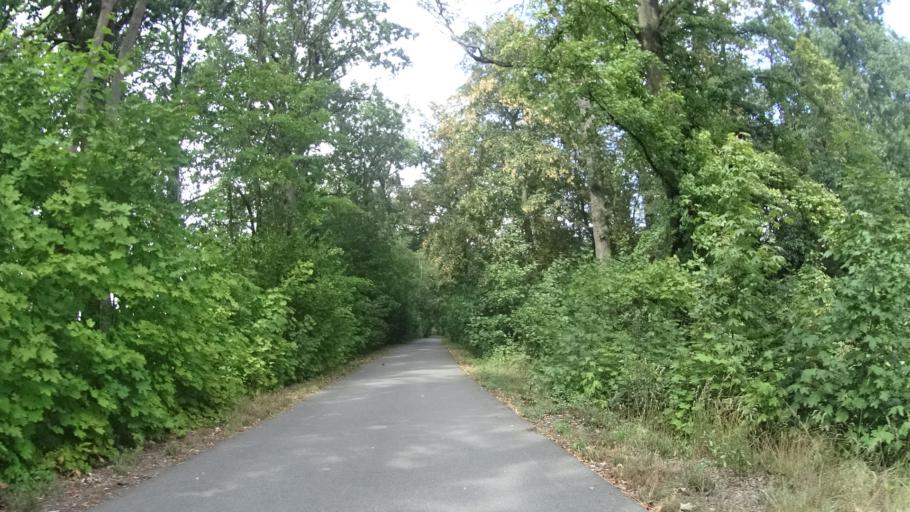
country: CZ
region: Olomoucky
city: Horka nad Moravou
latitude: 49.6445
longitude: 17.1972
